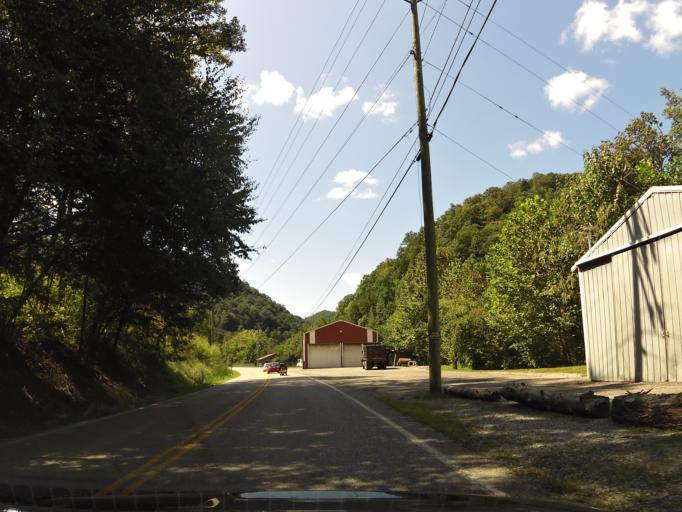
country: US
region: Kentucky
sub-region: Harlan County
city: Loyall
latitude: 36.9817
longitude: -83.4022
